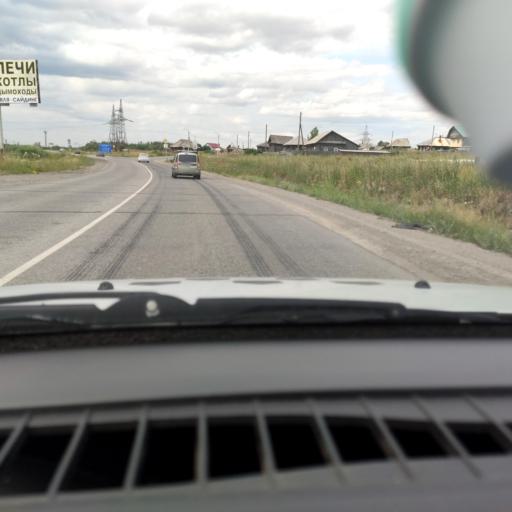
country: RU
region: Perm
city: Solikamsk
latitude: 59.5886
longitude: 56.7688
